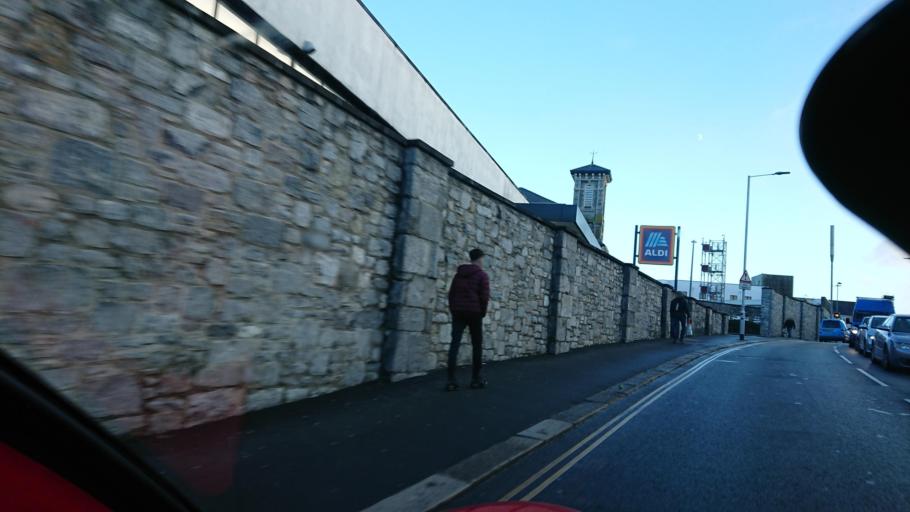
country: GB
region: England
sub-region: Plymouth
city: Plymouth
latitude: 50.3795
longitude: -4.1316
